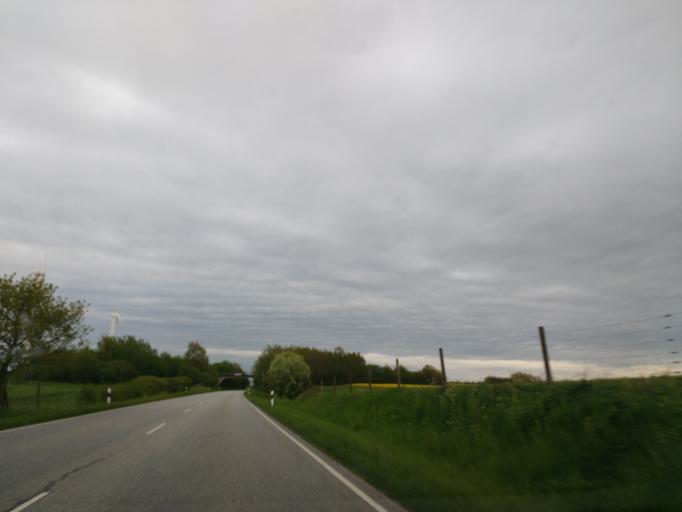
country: DE
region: Schleswig-Holstein
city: Brodersby
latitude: 54.6464
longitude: 9.9585
